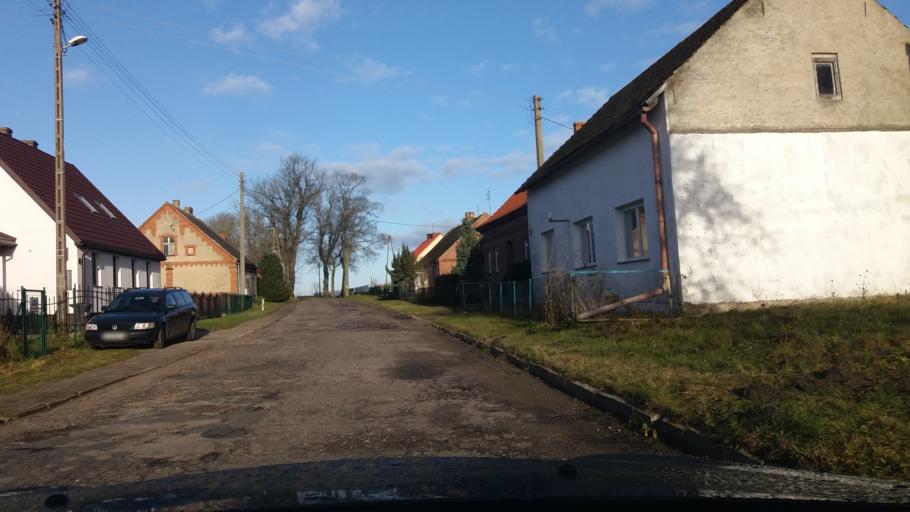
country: PL
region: West Pomeranian Voivodeship
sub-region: Powiat choszczenski
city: Drawno
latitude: 53.1788
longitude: 15.8042
